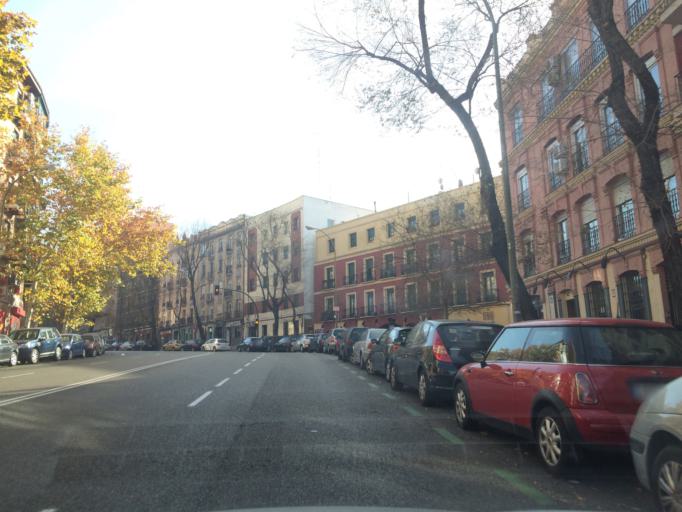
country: ES
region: Madrid
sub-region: Provincia de Madrid
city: Madrid
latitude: 40.4091
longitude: -3.7170
